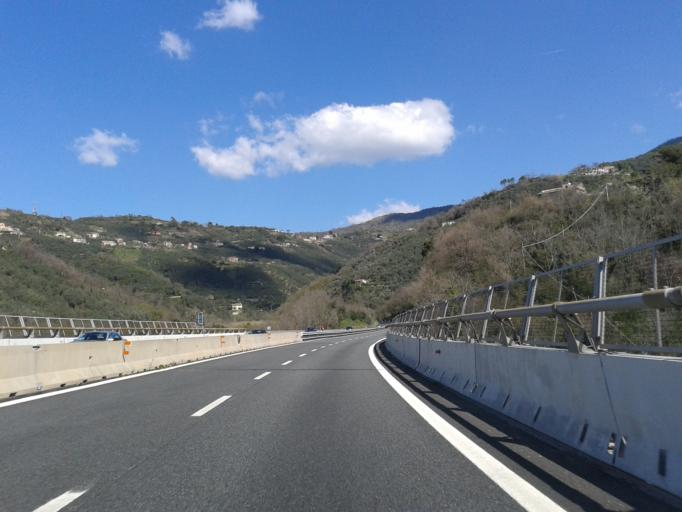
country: IT
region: Liguria
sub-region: Provincia di Genova
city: Sestri Levante
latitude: 44.2961
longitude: 9.3838
